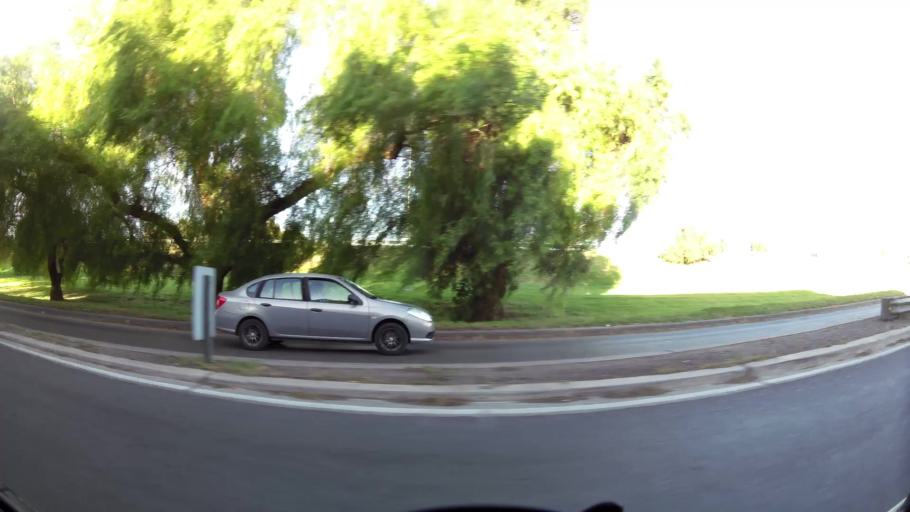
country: AR
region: San Juan
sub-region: Departamento de Santa Lucia
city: Santa Lucia
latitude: -31.5424
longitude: -68.5042
